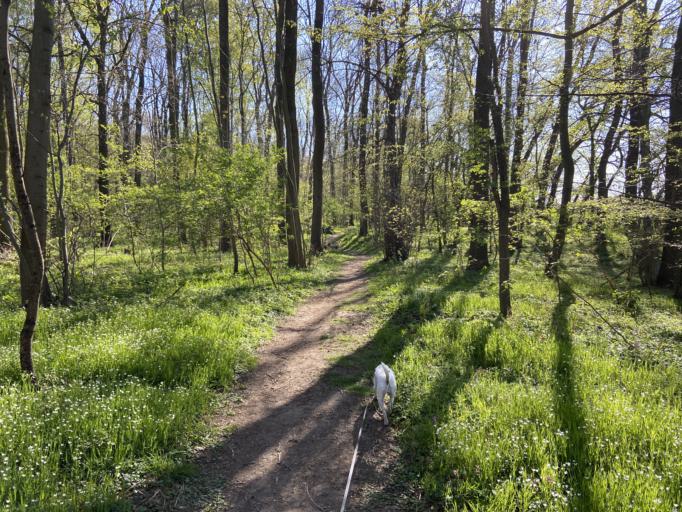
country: DE
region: Saxony-Anhalt
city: Zeitz
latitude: 51.0669
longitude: 12.1523
